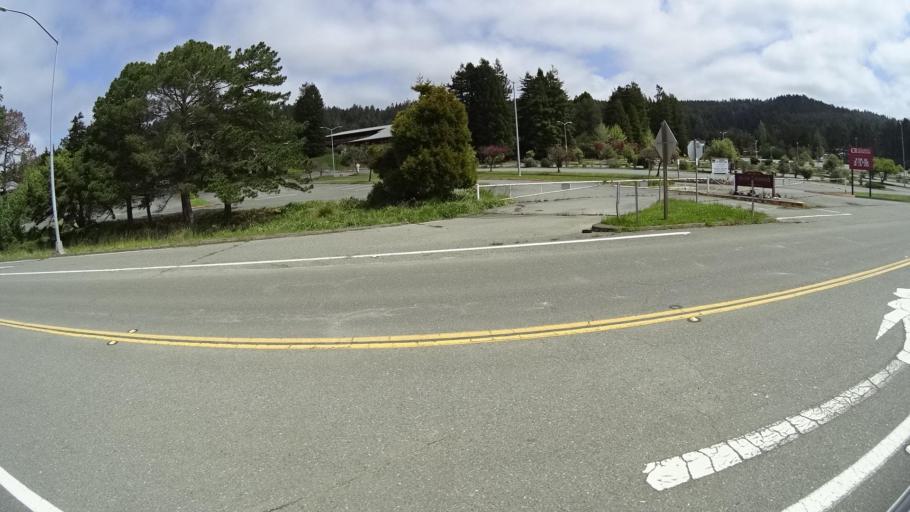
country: US
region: California
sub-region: Humboldt County
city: Humboldt Hill
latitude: 40.6968
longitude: -124.2008
